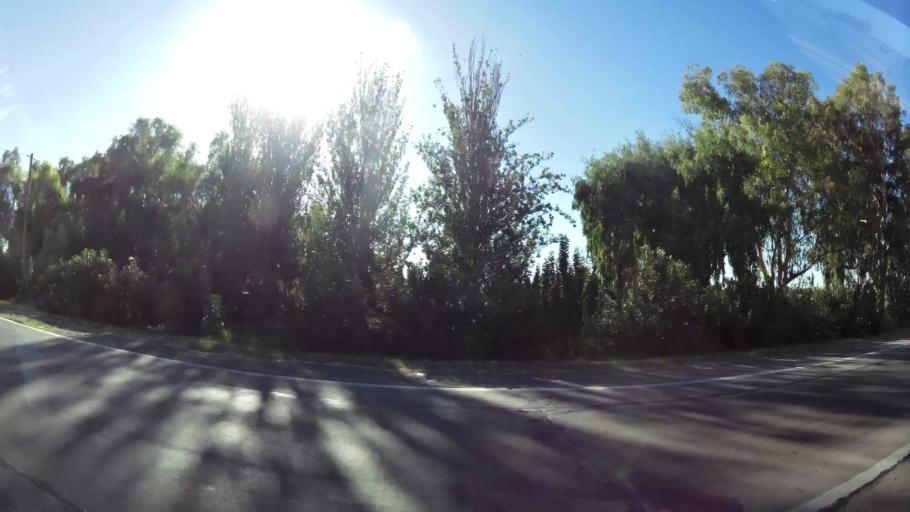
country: AR
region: Mendoza
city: Las Heras
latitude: -32.8320
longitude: -68.8067
